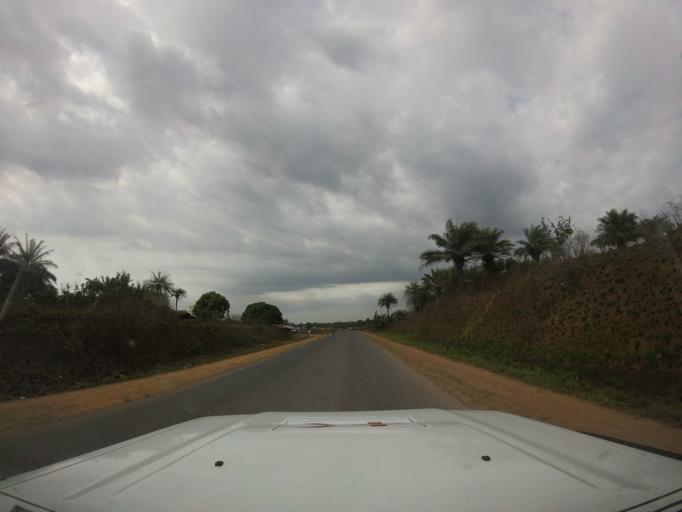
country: LR
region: Montserrado
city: Monrovia
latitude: 6.5096
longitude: -10.8214
